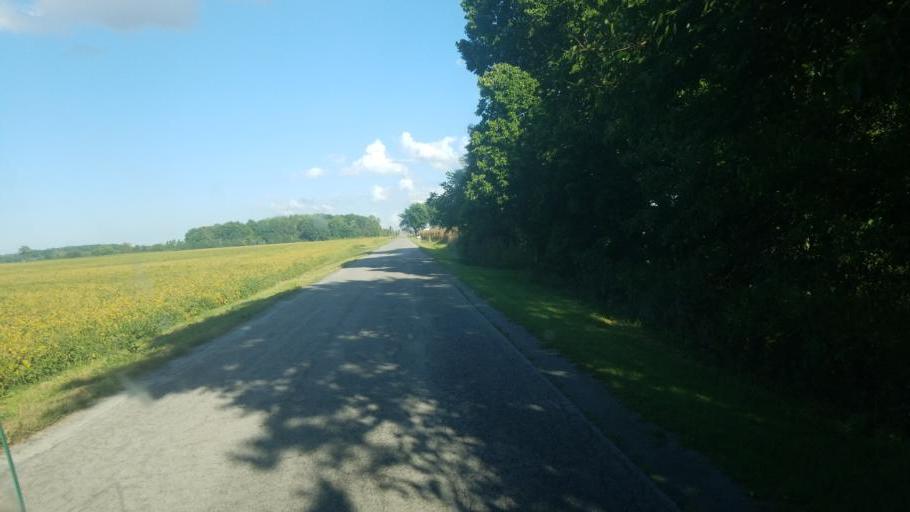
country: US
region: Ohio
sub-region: Hancock County
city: Arlington
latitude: 40.9359
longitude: -83.6681
